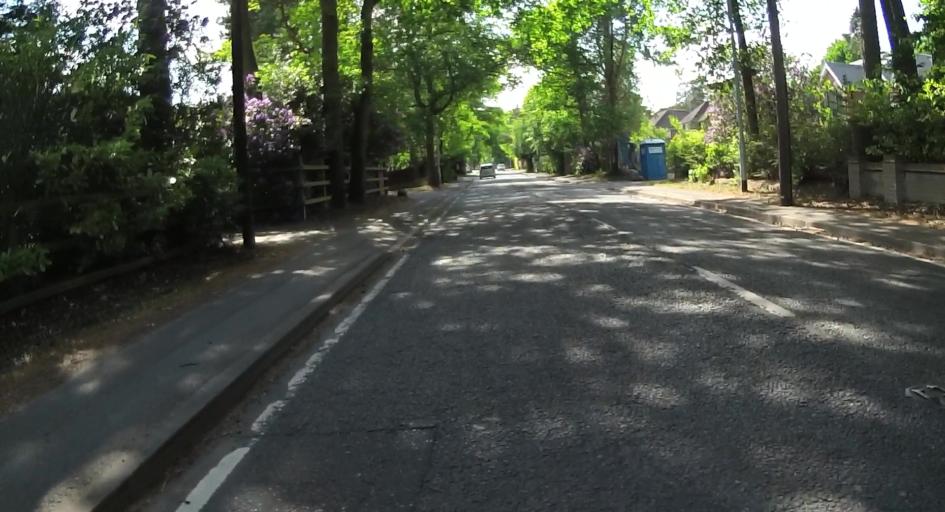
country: GB
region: England
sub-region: Wokingham
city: Finchampstead
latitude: 51.3792
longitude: -0.8343
